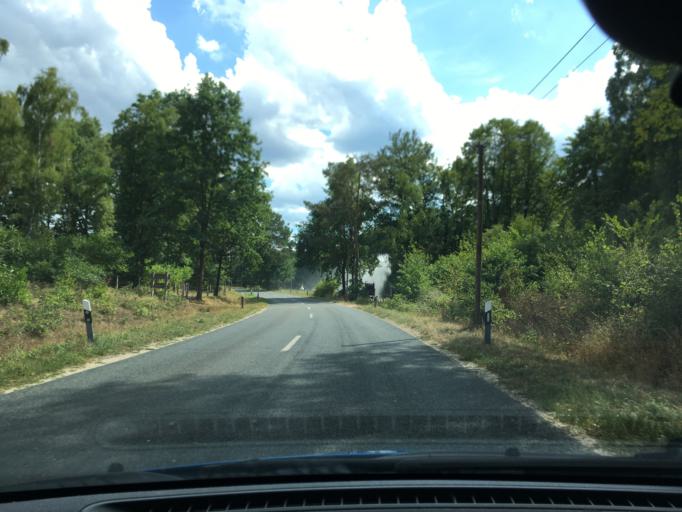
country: DE
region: Lower Saxony
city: Rehlingen
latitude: 53.0904
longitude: 10.2035
